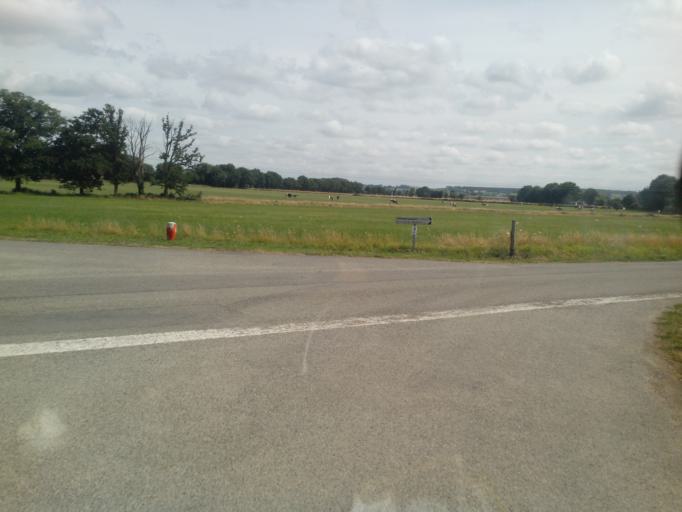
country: FR
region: Brittany
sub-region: Departement d'Ille-et-Vilaine
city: Messac
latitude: 47.8154
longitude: -1.8122
